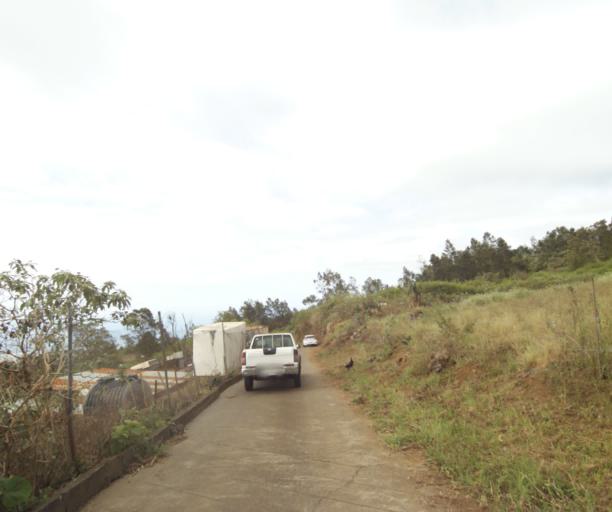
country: RE
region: Reunion
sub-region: Reunion
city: Saint-Paul
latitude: -21.0107
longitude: 55.3484
